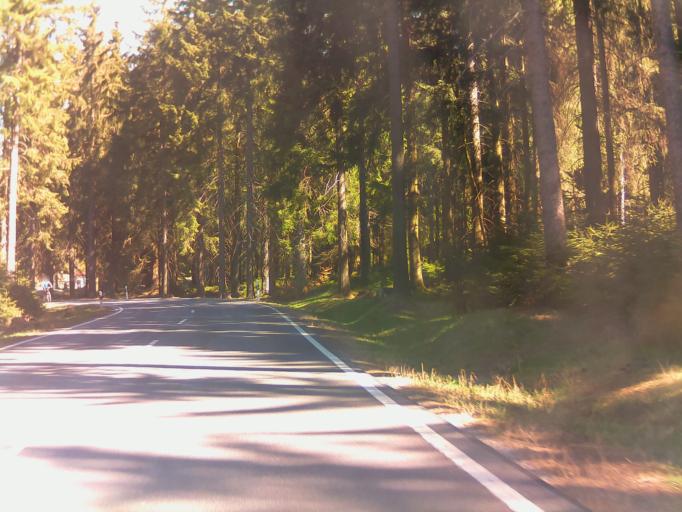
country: DE
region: Thuringia
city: Stutzerbach
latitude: 50.6083
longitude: 10.8943
